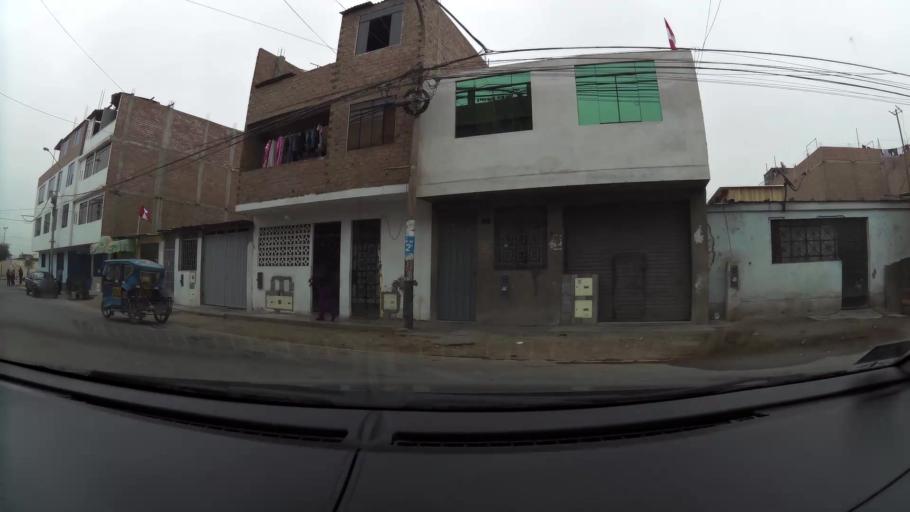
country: PE
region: Lima
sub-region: Lima
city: Independencia
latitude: -11.9623
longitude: -77.0796
